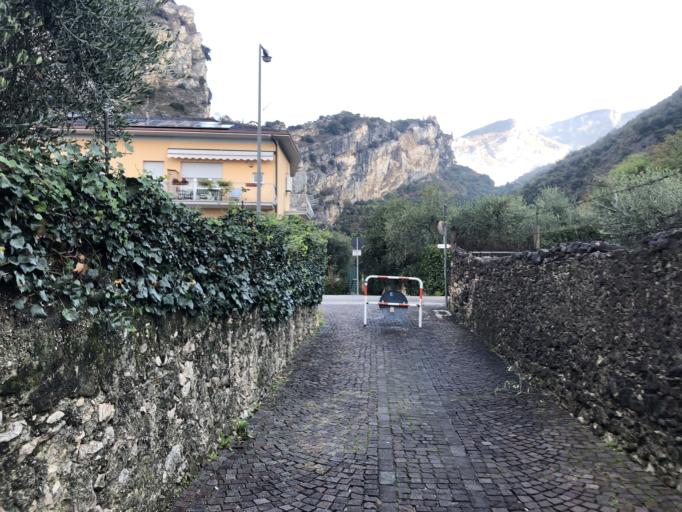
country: IT
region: Trentino-Alto Adige
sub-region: Provincia di Trento
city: Torbole sul Garda
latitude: 45.8696
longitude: 10.8797
